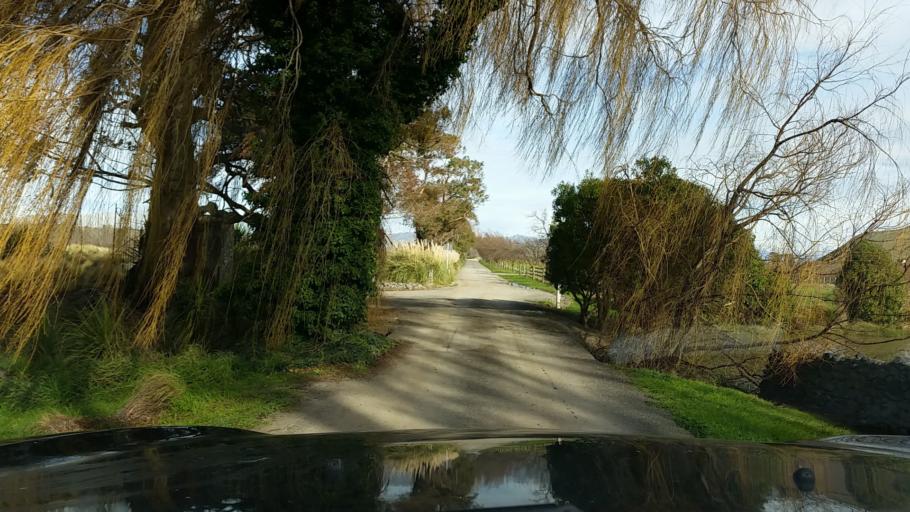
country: NZ
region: Marlborough
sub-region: Marlborough District
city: Blenheim
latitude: -41.6177
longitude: 174.1006
